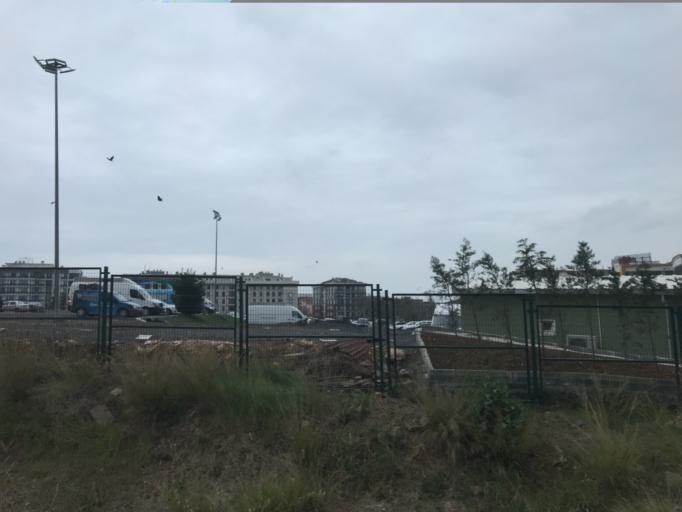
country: TR
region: Istanbul
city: Icmeler
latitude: 40.8438
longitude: 29.3023
